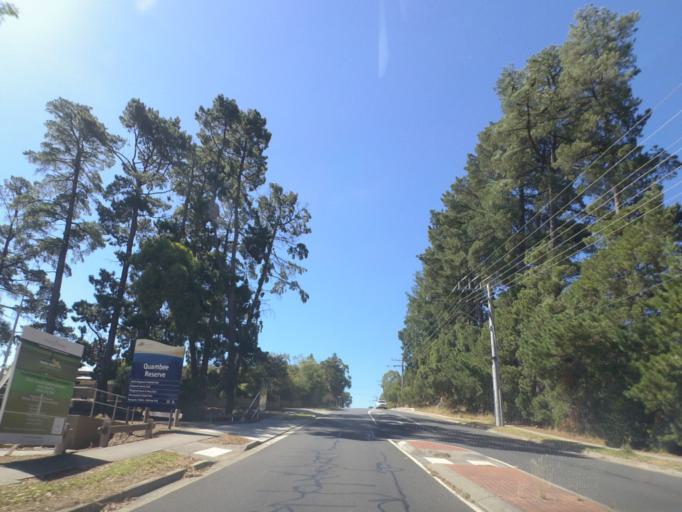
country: AU
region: Victoria
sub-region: Maroondah
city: Warranwood
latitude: -37.7830
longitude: 145.2487
